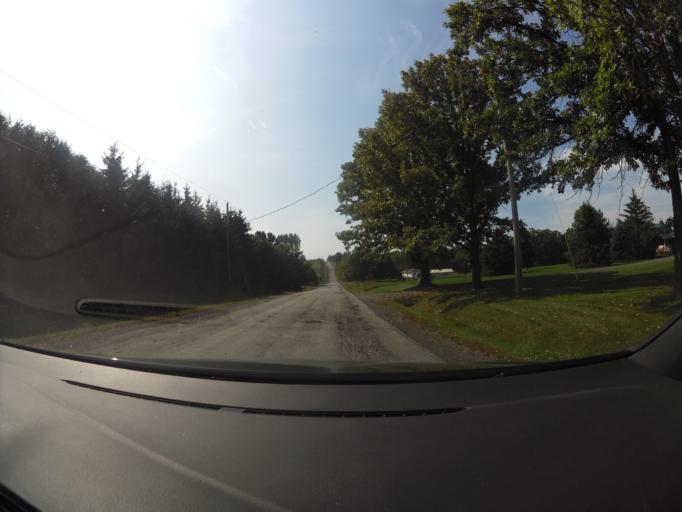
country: CA
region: Ontario
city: Carleton Place
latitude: 45.3090
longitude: -76.2010
